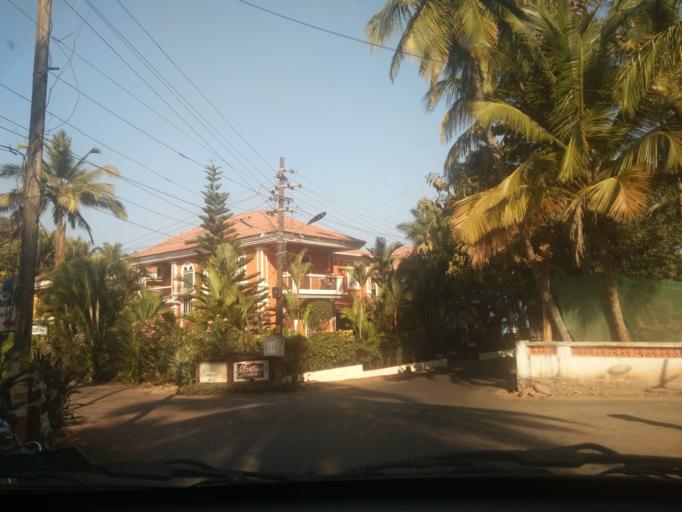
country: IN
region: Goa
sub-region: South Goa
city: Colva
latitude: 15.3030
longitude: 73.9145
